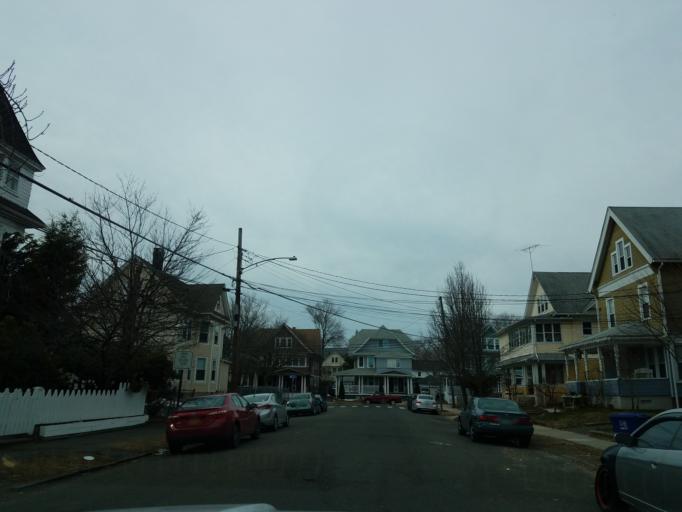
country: US
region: Connecticut
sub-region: Fairfield County
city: Bridgeport
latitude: 41.1786
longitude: -73.2101
